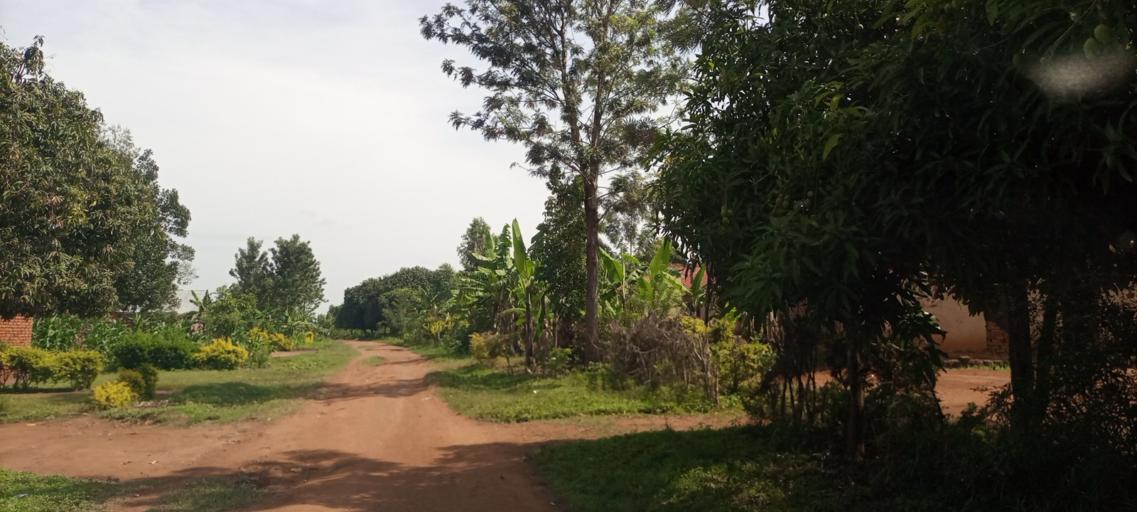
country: UG
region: Eastern Region
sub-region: Mbale District
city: Mbale
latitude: 1.1302
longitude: 34.0238
